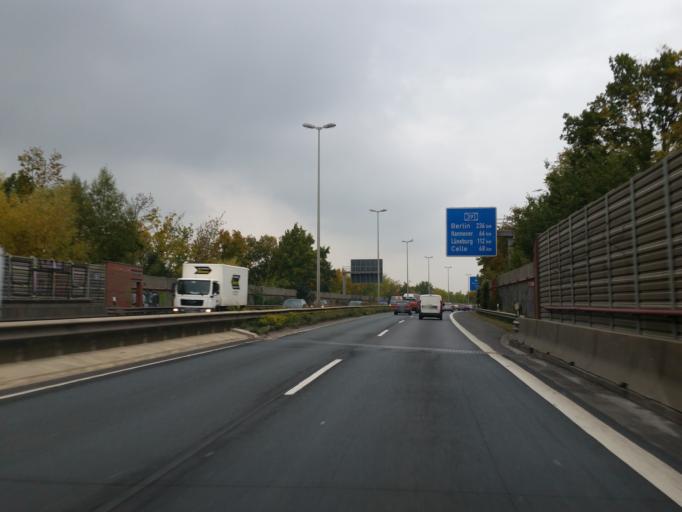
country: DE
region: Lower Saxony
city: Braunschweig
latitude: 52.2606
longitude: 10.4878
